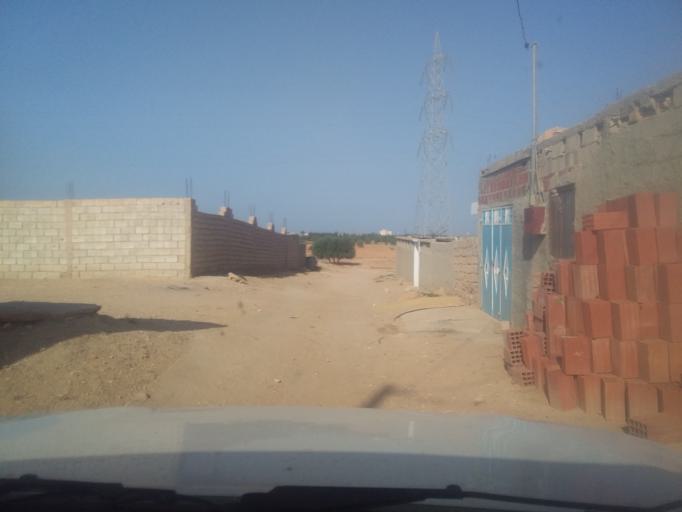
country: TN
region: Qabis
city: Matmata
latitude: 33.5843
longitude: 10.2699
